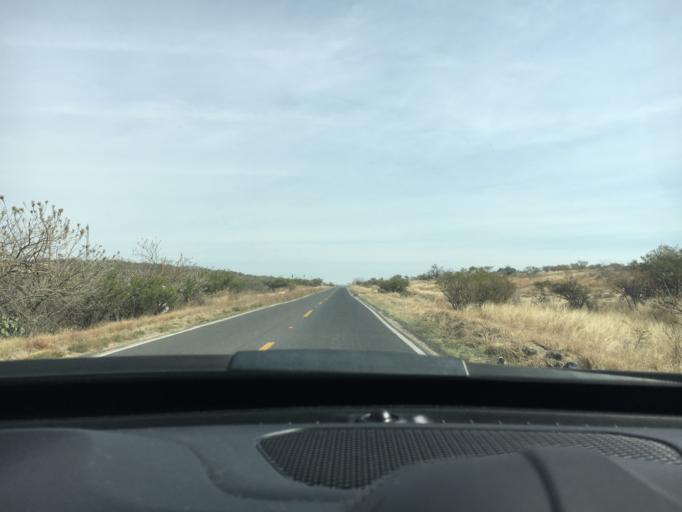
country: MX
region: Guanajuato
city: Duarte
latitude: 21.0591
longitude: -101.5069
